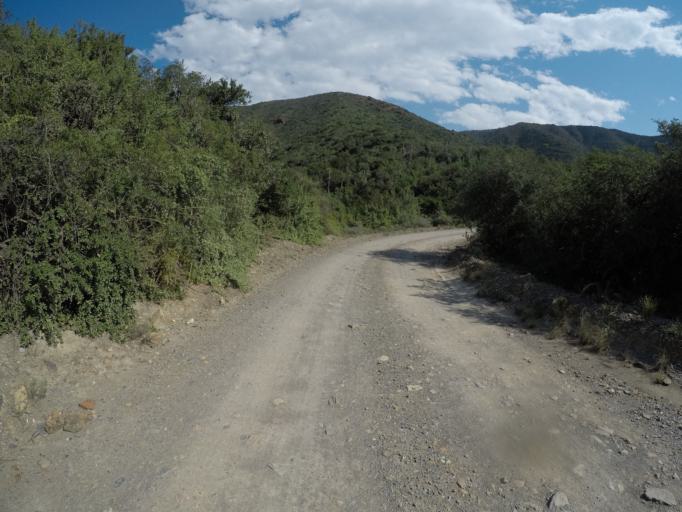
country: ZA
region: Eastern Cape
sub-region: Cacadu District Municipality
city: Kareedouw
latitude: -33.6535
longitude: 24.3537
